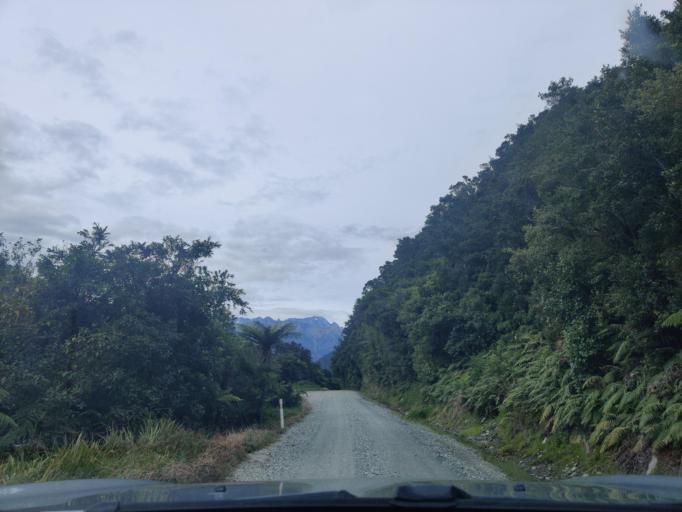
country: NZ
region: West Coast
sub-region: Westland District
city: Hokitika
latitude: -43.2883
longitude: 170.4046
